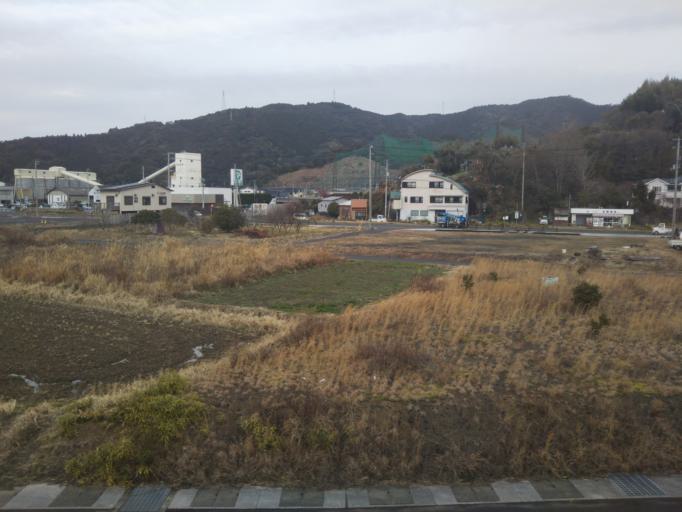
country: JP
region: Kochi
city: Nakamura
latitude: 32.9845
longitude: 132.9608
